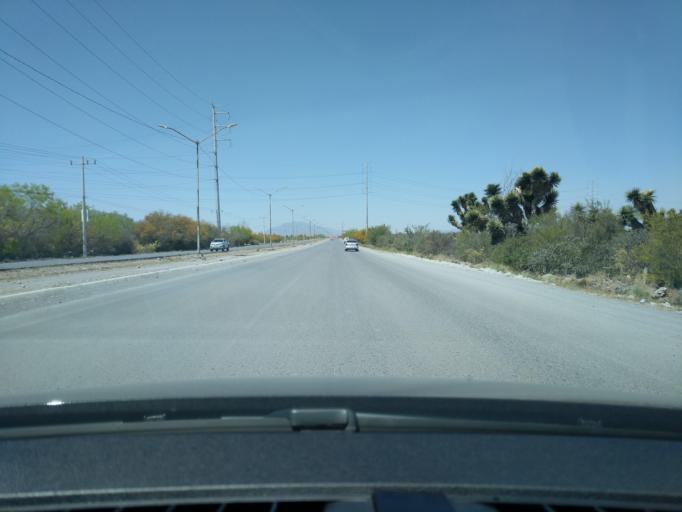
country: MX
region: Nuevo Leon
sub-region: Salinas Victoria
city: Emiliano Zapata
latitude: 25.9178
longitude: -100.2697
